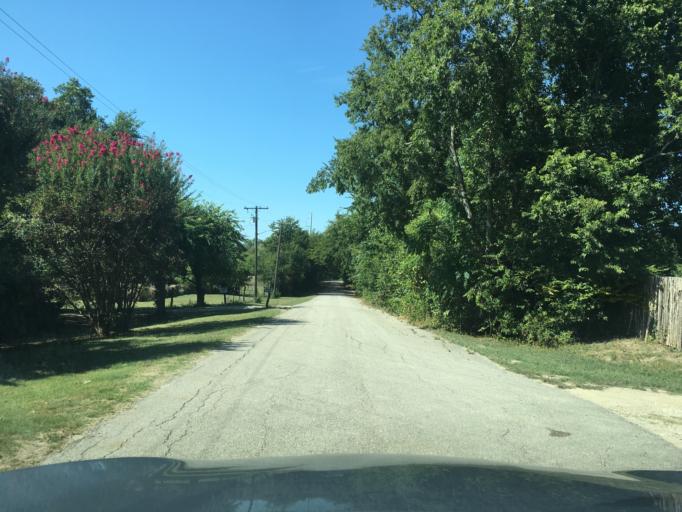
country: US
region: Texas
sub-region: Dallas County
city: Sachse
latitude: 32.9621
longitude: -96.6079
